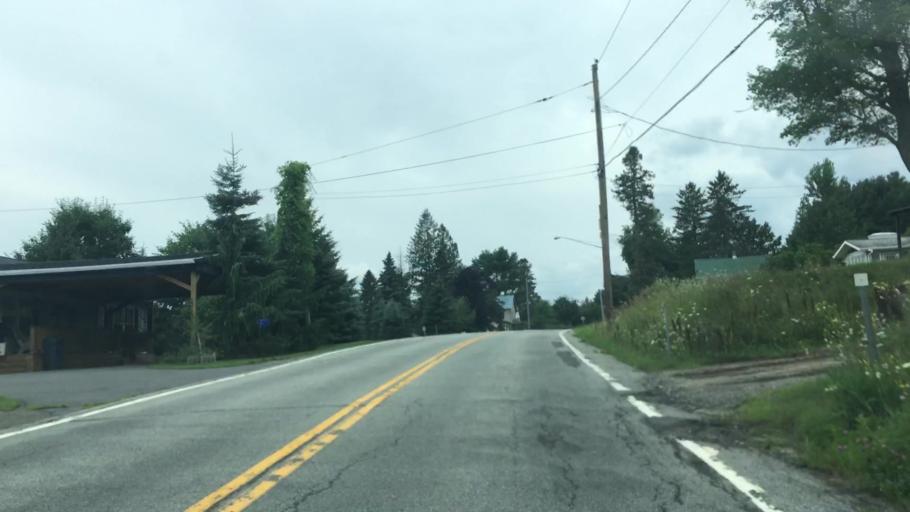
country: US
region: New York
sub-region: Essex County
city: Elizabethtown
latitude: 44.3844
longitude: -73.7145
